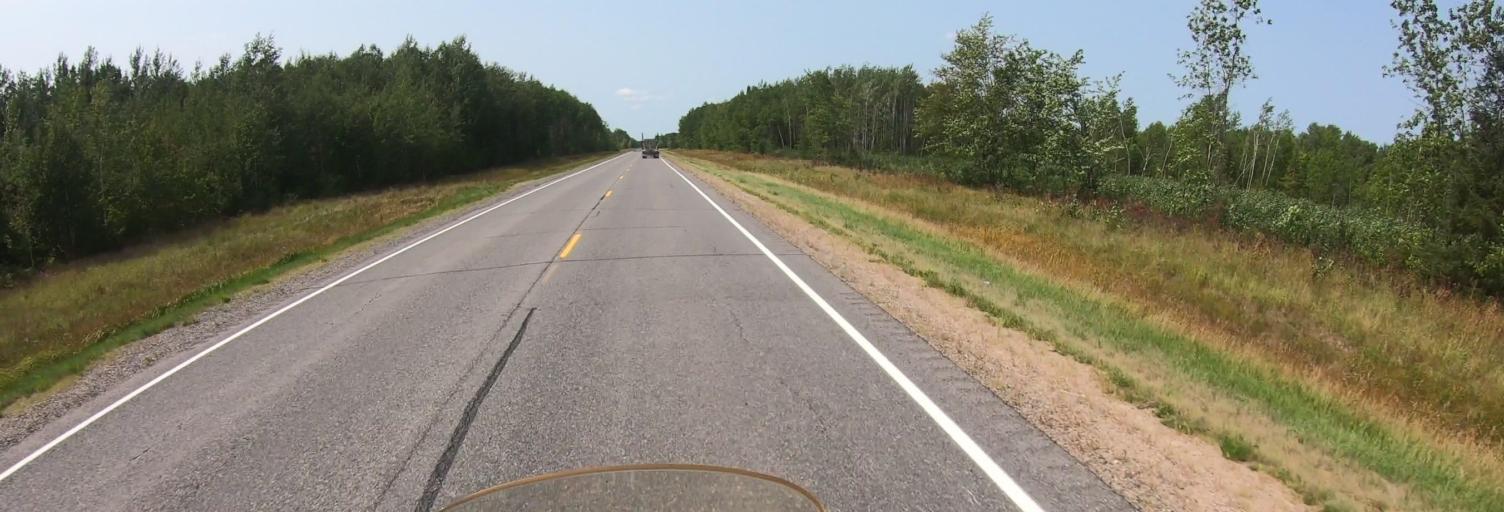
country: US
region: Minnesota
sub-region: Koochiching County
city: International Falls
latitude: 48.5127
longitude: -93.7595
